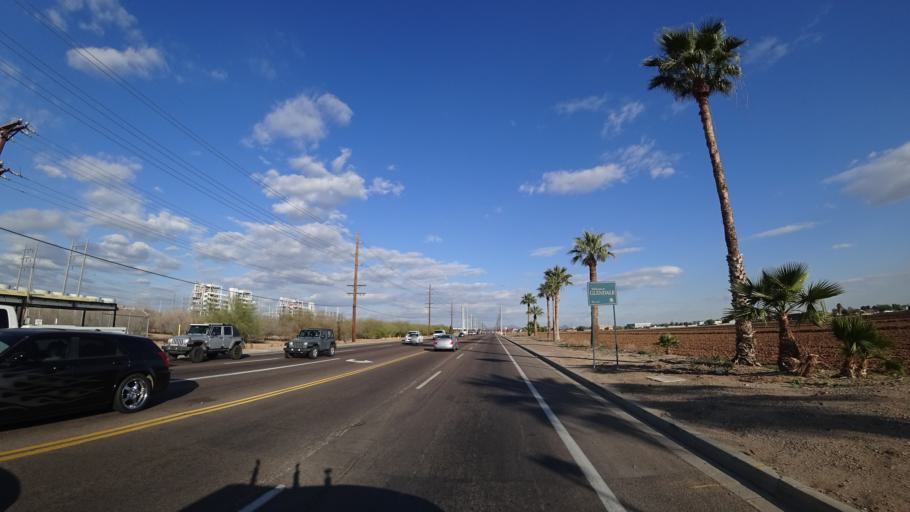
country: US
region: Arizona
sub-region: Maricopa County
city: Peoria
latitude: 33.5524
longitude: -112.2199
